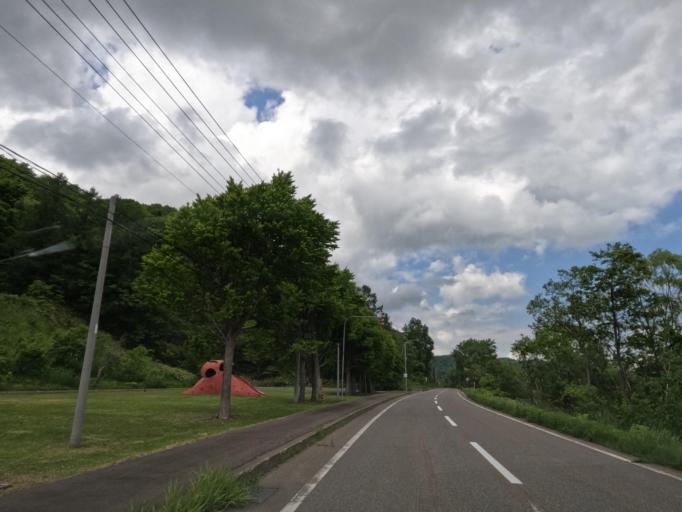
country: JP
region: Hokkaido
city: Takikawa
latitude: 43.5824
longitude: 141.7280
